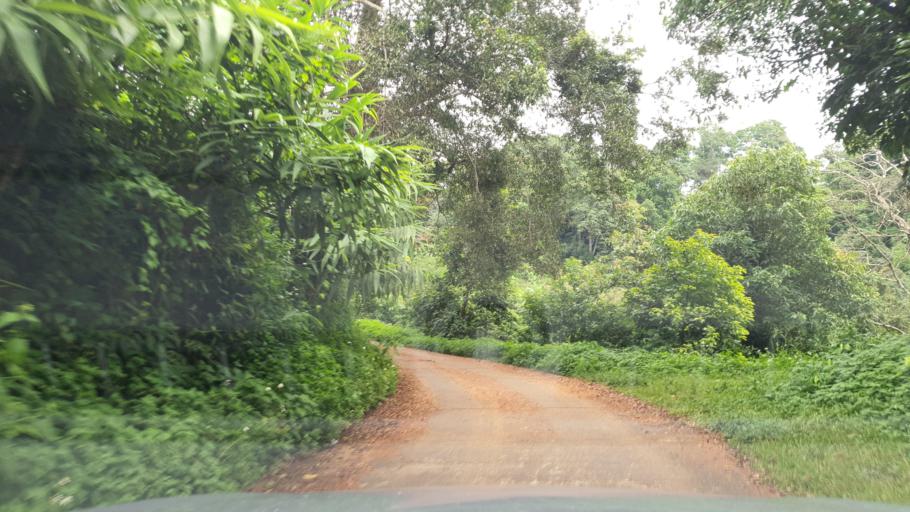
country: TH
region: Chiang Mai
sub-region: Amphoe Chiang Dao
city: Chiang Dao
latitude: 19.2564
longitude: 98.9209
